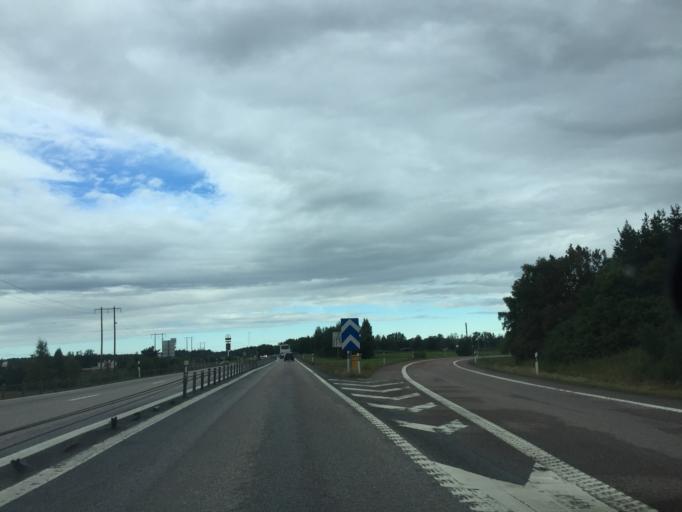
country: SE
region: Soedermanland
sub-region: Eskilstuna Kommun
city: Torshalla
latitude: 59.3915
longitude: 16.4738
